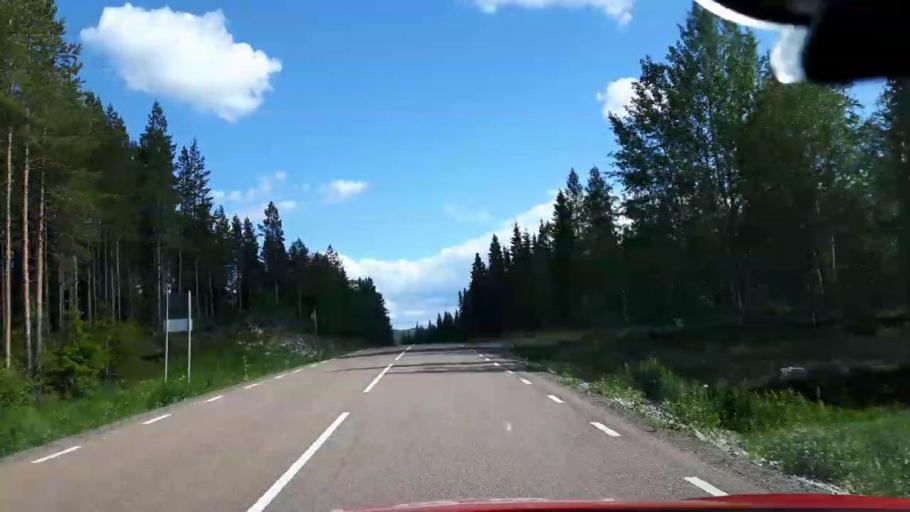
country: SE
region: Jaemtland
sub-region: Krokoms Kommun
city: Valla
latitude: 64.0600
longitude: 14.1537
